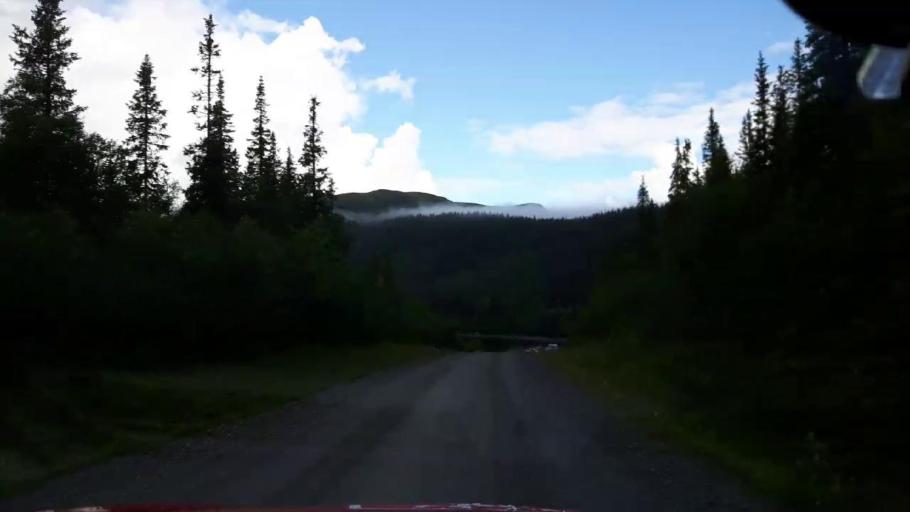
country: NO
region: Nordland
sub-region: Hattfjelldal
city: Hattfjelldal
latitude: 64.8852
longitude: 14.7653
